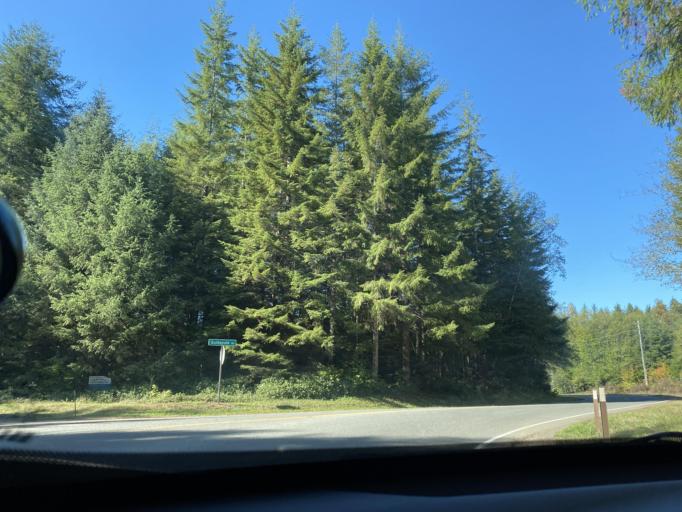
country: US
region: Washington
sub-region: Clallam County
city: Forks
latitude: 47.9525
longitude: -124.4606
